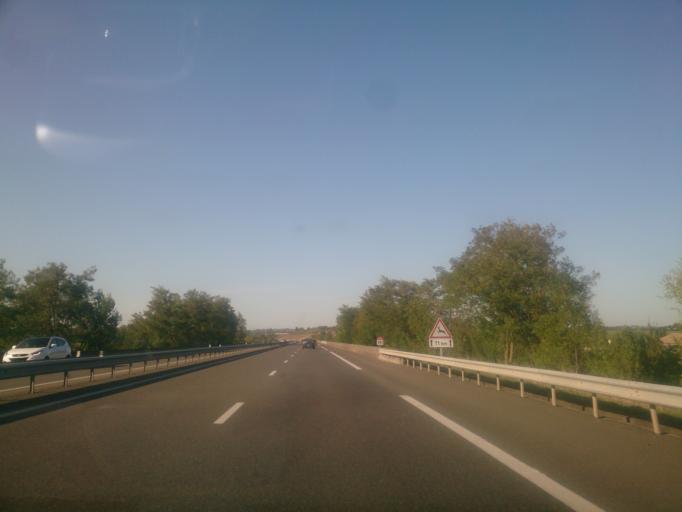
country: FR
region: Midi-Pyrenees
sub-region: Departement du Tarn-et-Garonne
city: Caussade
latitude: 44.1994
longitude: 1.5394
